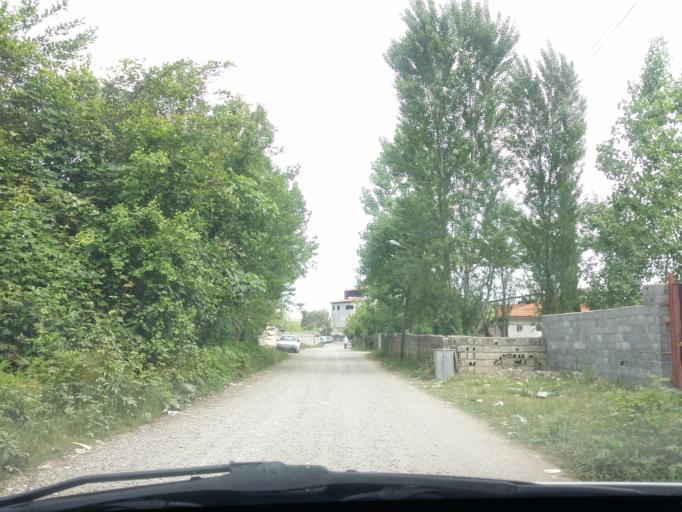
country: IR
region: Mazandaran
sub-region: Nowshahr
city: Nowshahr
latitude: 36.6218
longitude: 51.4941
